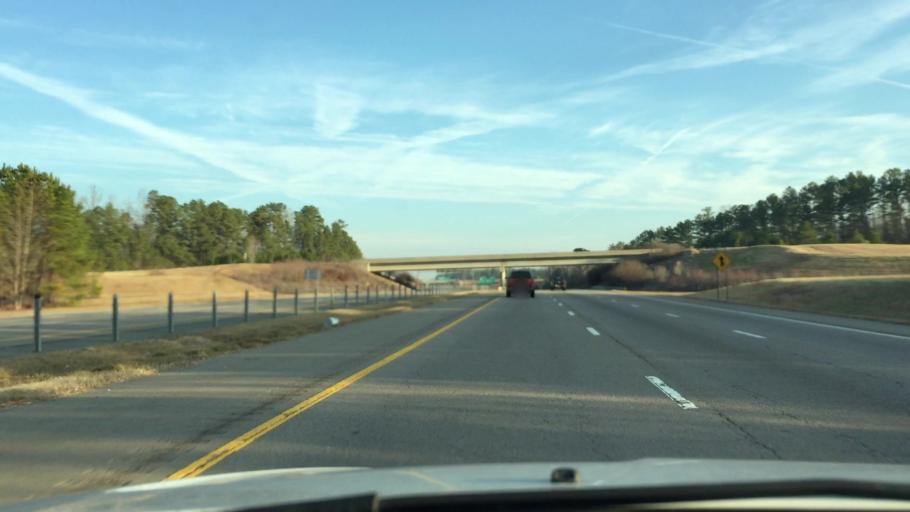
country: US
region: North Carolina
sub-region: Lee County
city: Sanford
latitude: 35.5011
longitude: -79.1920
